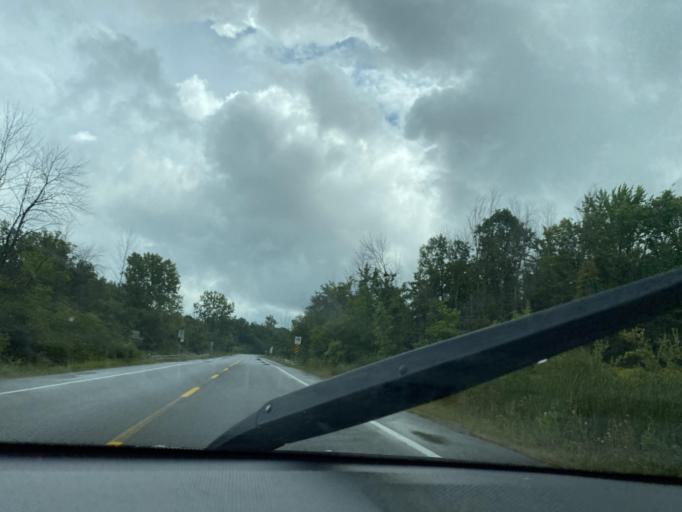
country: CA
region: Quebec
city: Baie-D'Urfe
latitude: 45.4451
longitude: -73.9169
